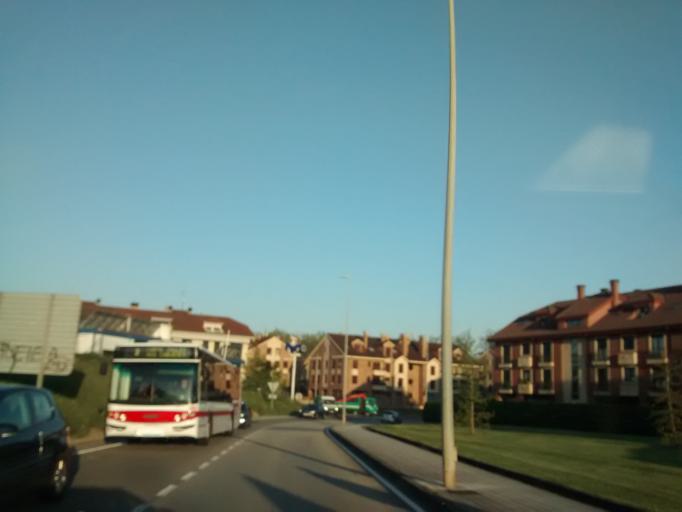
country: ES
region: Asturias
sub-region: Province of Asturias
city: Gijon
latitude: 43.5249
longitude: -5.6406
